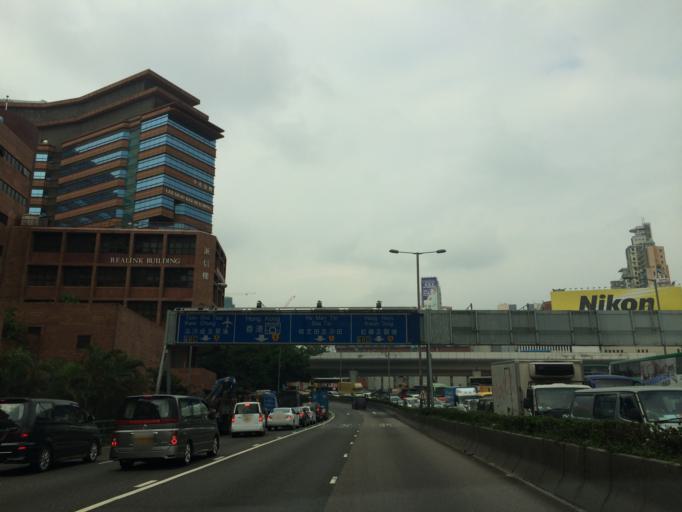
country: HK
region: Kowloon City
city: Kowloon
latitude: 22.3046
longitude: 114.1811
